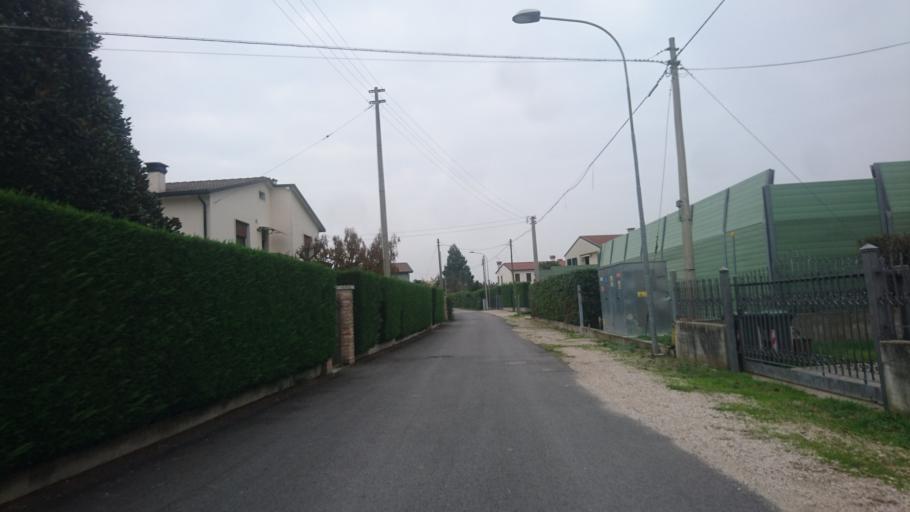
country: IT
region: Veneto
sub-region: Provincia di Padova
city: Oltre Brenta
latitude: 45.4066
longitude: 11.9918
